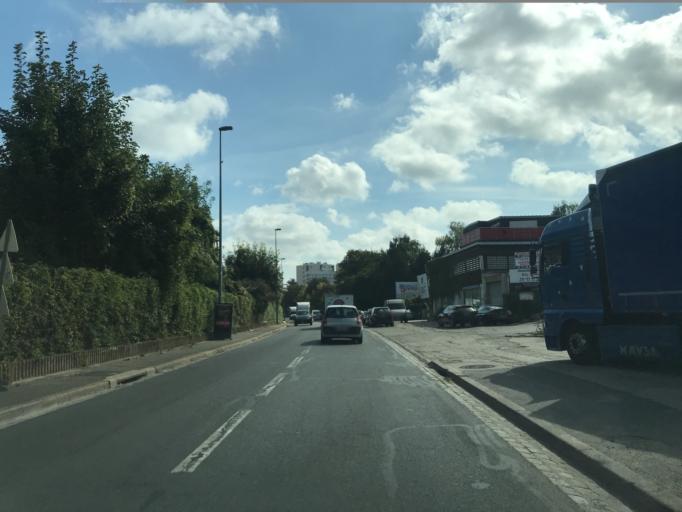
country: FR
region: Ile-de-France
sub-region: Departement de Seine-Saint-Denis
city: Bobigny
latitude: 48.9052
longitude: 2.4355
